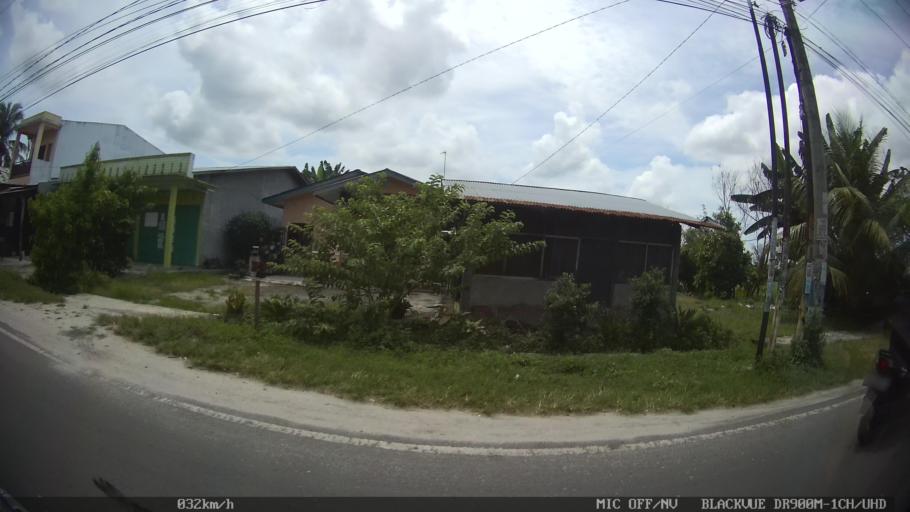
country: ID
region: North Sumatra
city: Percut
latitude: 3.5741
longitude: 98.8831
